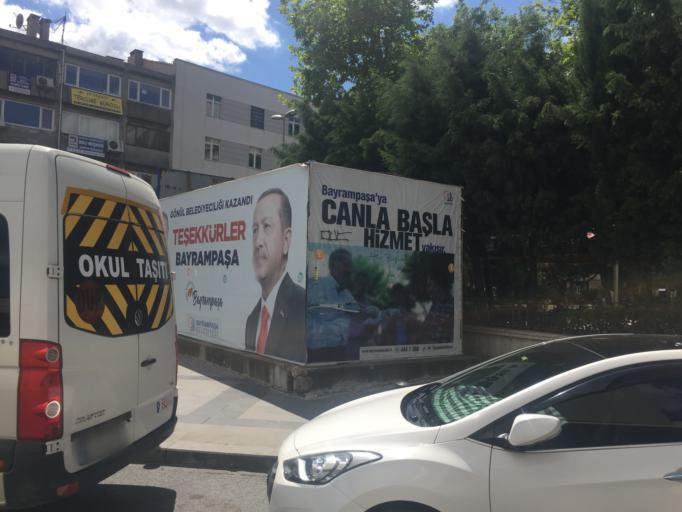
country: TR
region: Istanbul
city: merter keresteciler
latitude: 41.0348
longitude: 28.9119
